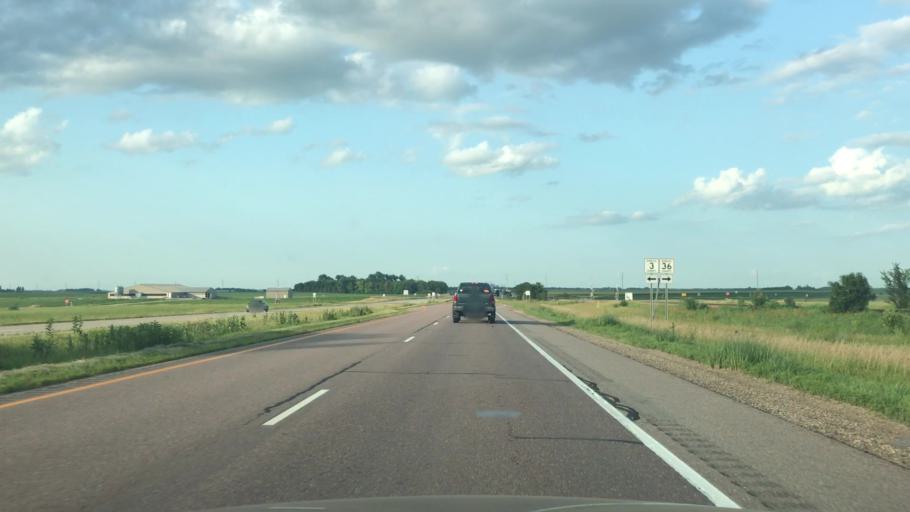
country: US
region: Minnesota
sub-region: Nobles County
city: Worthington
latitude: 43.6590
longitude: -95.5325
